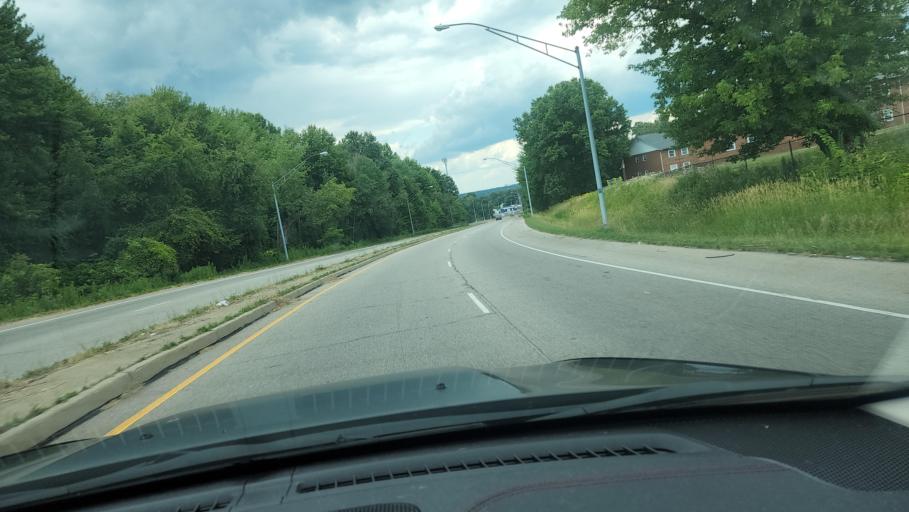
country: US
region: Ohio
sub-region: Mahoning County
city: Campbell
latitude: 41.0916
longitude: -80.6130
